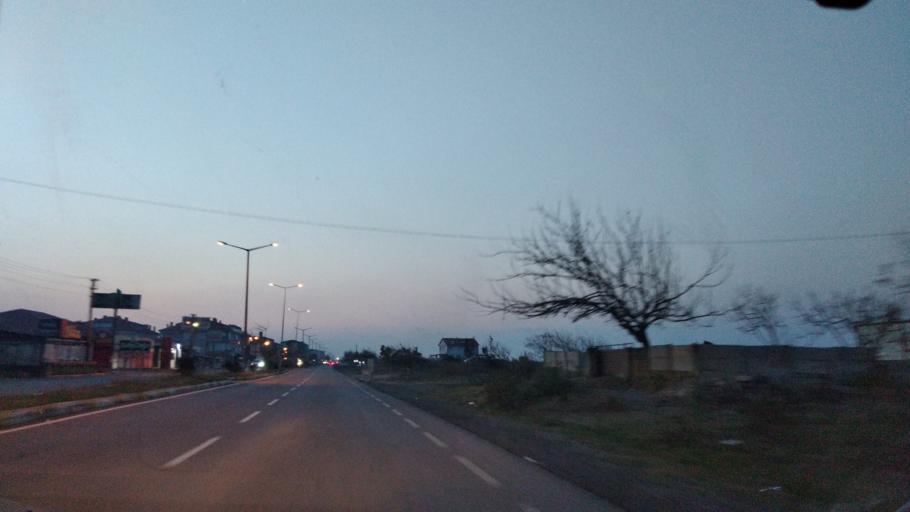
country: TR
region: Sakarya
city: Karasu
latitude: 41.0977
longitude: 30.7266
